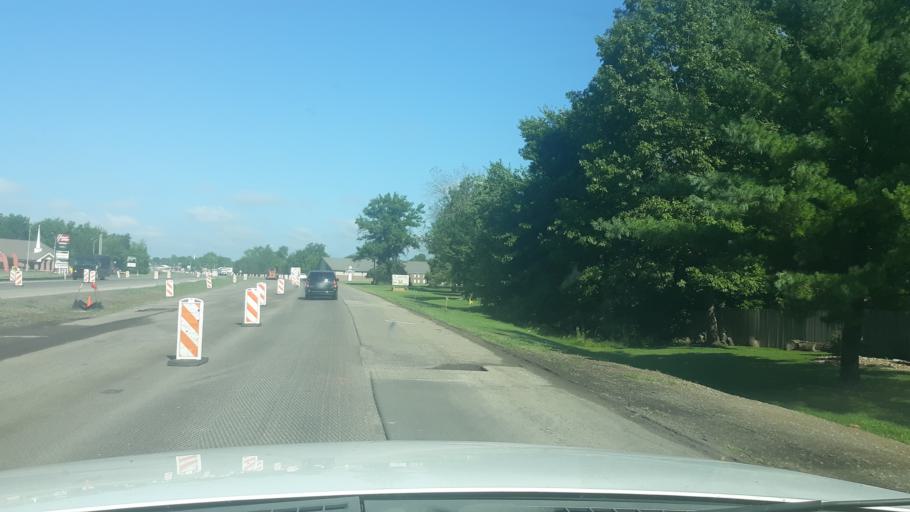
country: US
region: Illinois
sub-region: Williamson County
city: Marion
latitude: 37.7388
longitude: -88.9015
